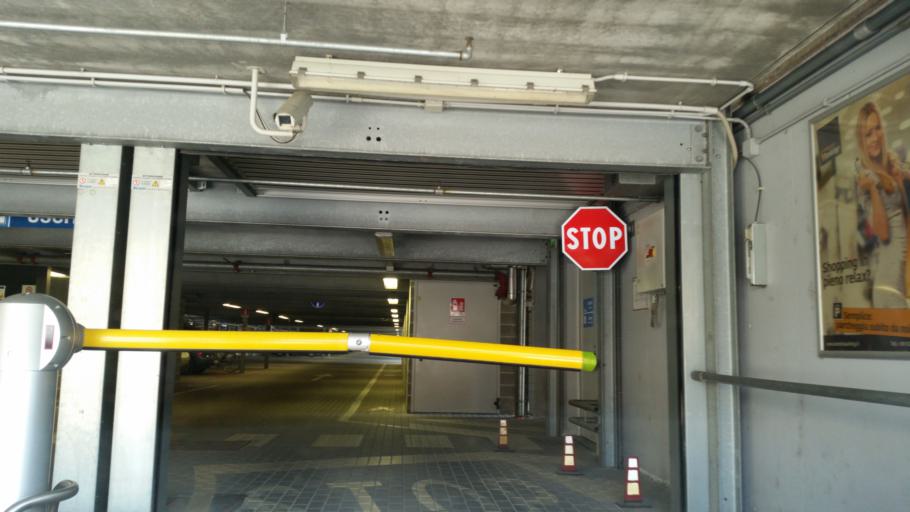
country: IT
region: Piedmont
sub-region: Provincia di Cuneo
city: Alba
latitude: 44.6976
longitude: 8.0311
